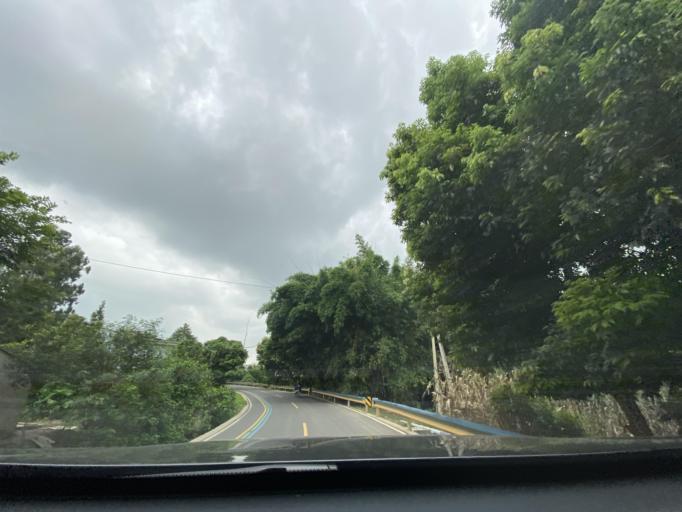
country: CN
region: Sichuan
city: Dongsheng
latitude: 30.4096
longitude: 103.9965
